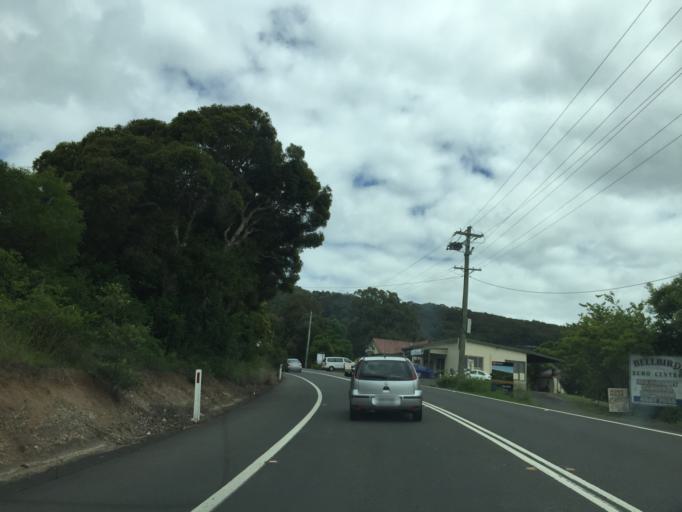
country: AU
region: New South Wales
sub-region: Hawkesbury
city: Richmond
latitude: -33.5425
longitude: 150.6453
